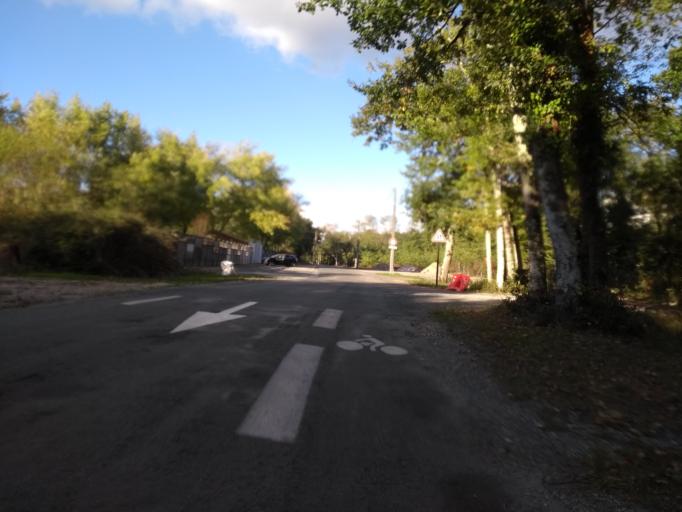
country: FR
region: Aquitaine
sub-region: Departement de la Gironde
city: Canejan
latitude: 44.7488
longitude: -0.6272
